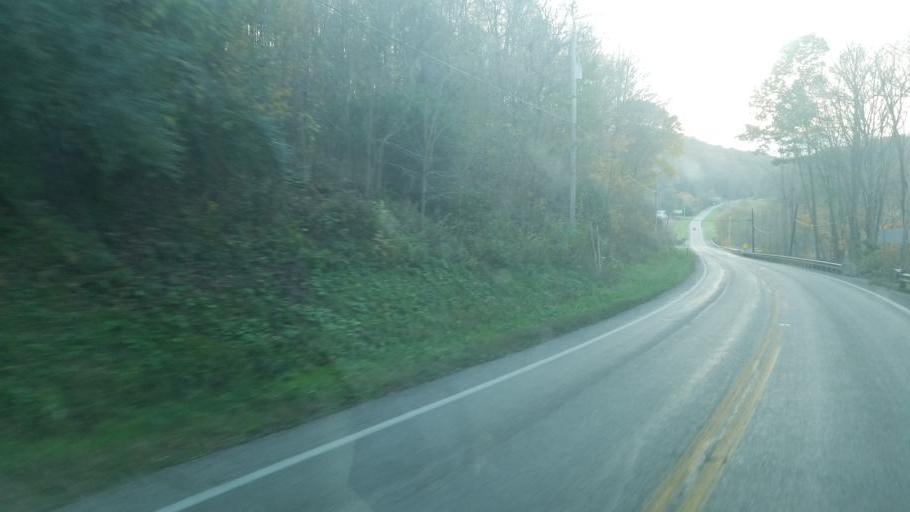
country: US
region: Ohio
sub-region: Ashland County
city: Loudonville
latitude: 40.6199
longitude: -82.1812
